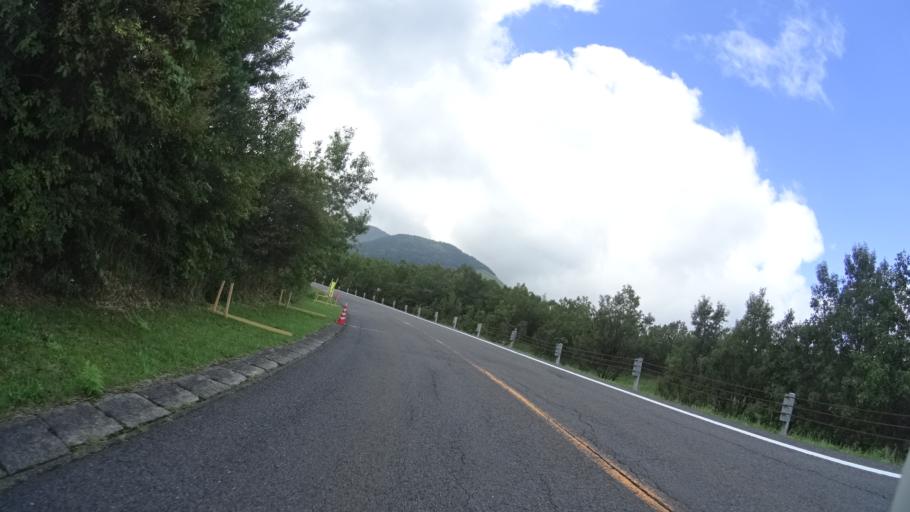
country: JP
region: Oita
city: Tsukawaki
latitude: 33.1304
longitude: 131.2288
